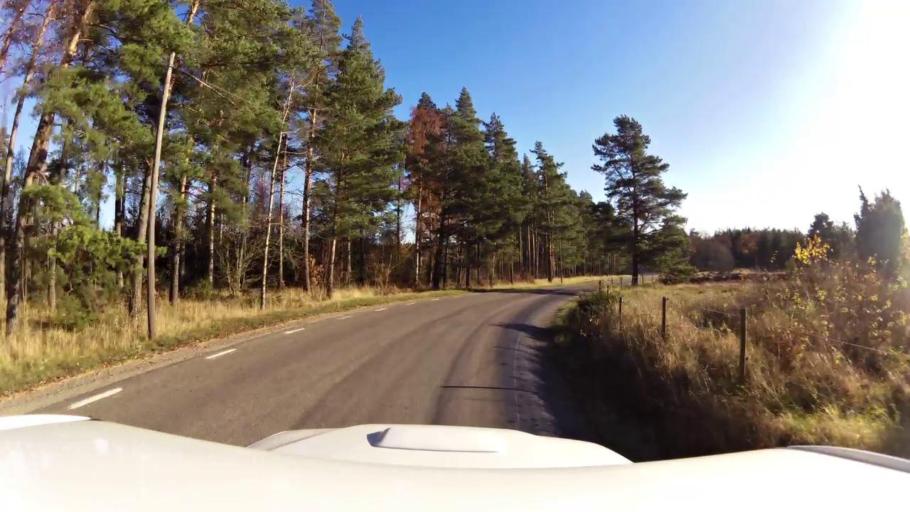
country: SE
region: OEstergoetland
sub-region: Linkopings Kommun
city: Linkoping
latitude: 58.3507
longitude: 15.5979
